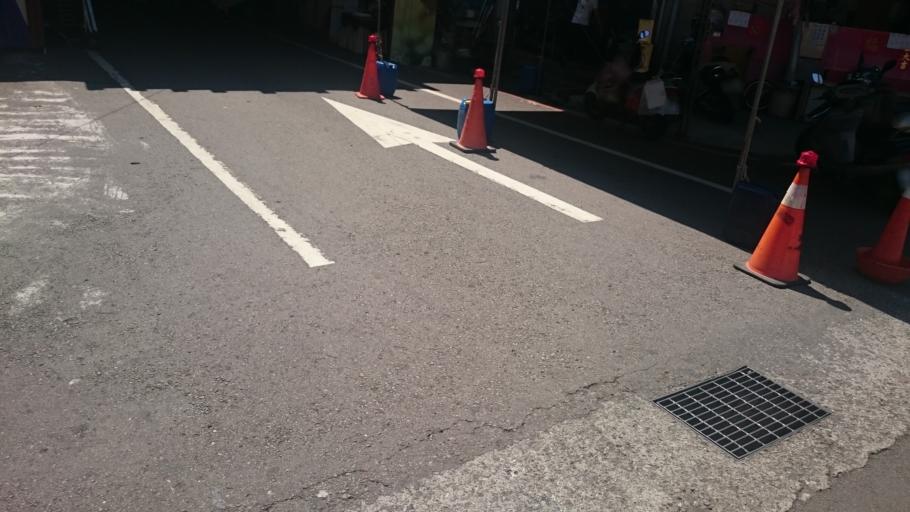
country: TW
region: Taiwan
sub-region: Miaoli
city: Miaoli
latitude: 24.5996
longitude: 120.9987
